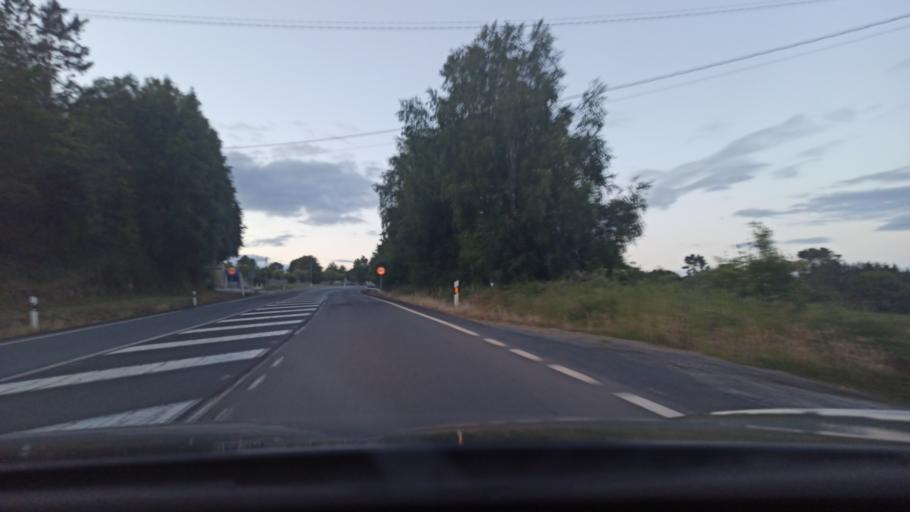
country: ES
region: Galicia
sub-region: Provincia de Lugo
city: Ourol
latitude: 42.9290
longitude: -7.6368
